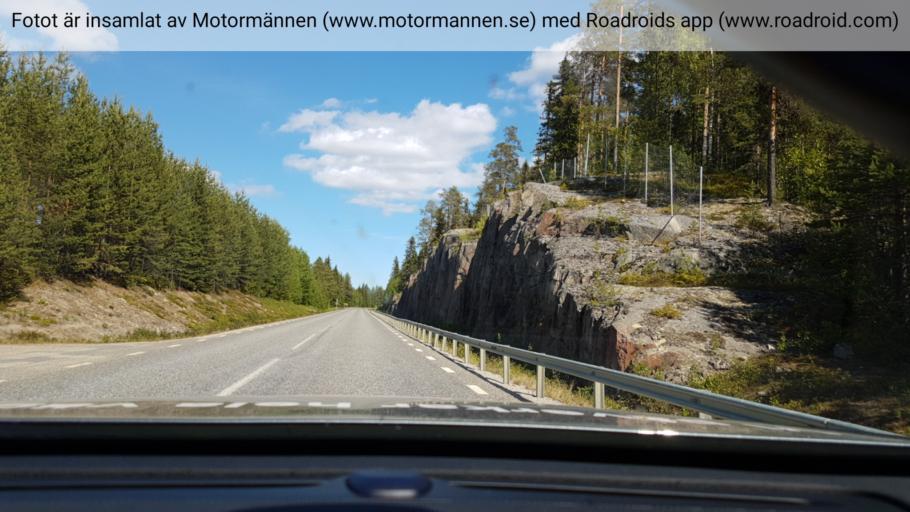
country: SE
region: Vaesterbotten
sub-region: Lycksele Kommun
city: Lycksele
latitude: 64.6133
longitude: 18.4494
